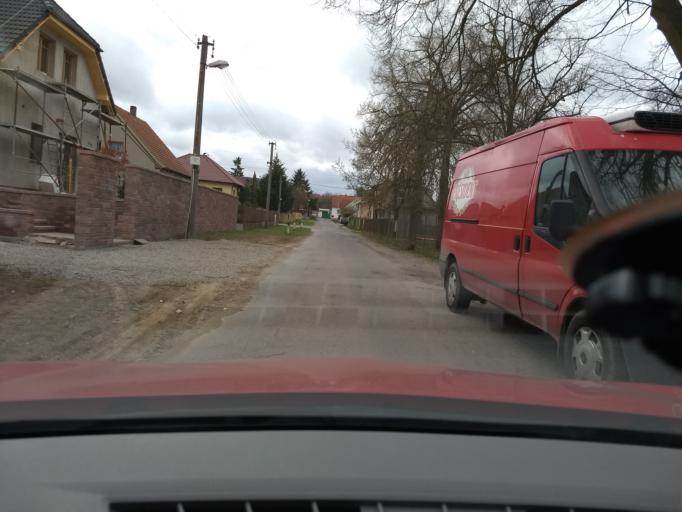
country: CZ
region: Central Bohemia
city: Unhost'
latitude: 50.0683
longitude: 14.1634
